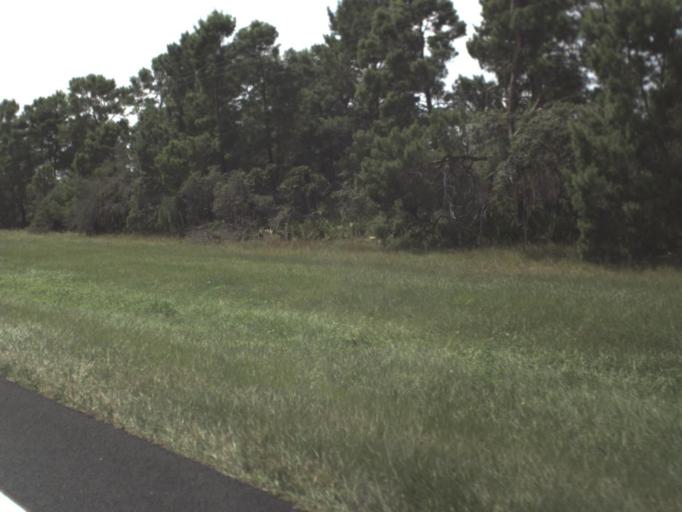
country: US
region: Florida
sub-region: Polk County
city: Frostproof
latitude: 27.7173
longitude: -81.5617
